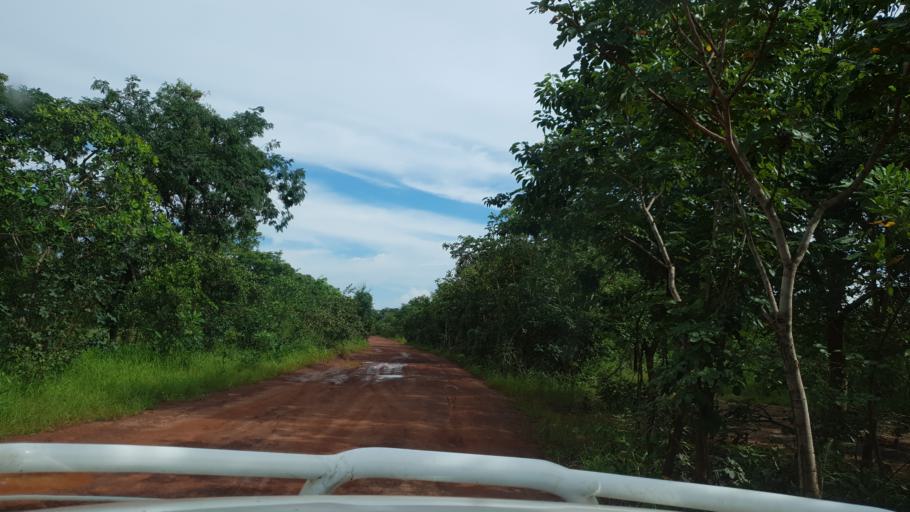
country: ML
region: Sikasso
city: Kolondieba
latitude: 10.7465
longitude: -6.9124
